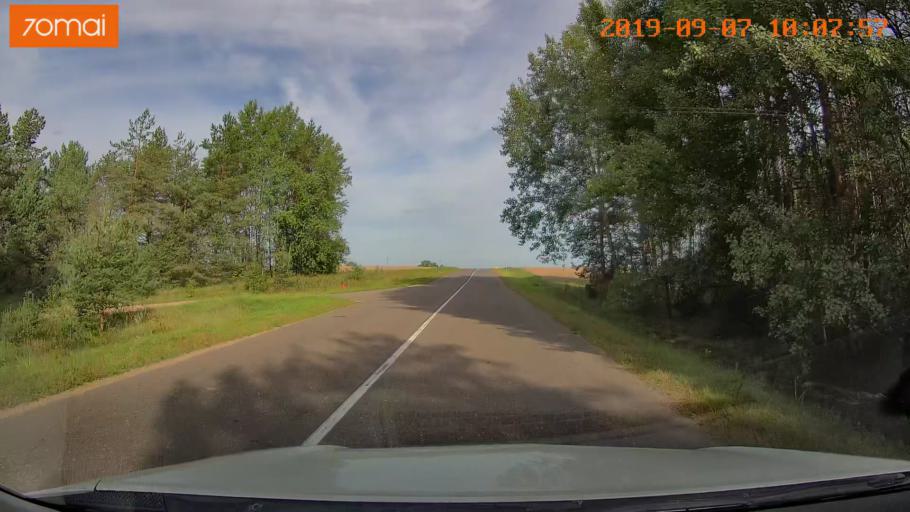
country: BY
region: Grodnenskaya
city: Voranava
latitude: 54.0822
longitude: 25.3935
